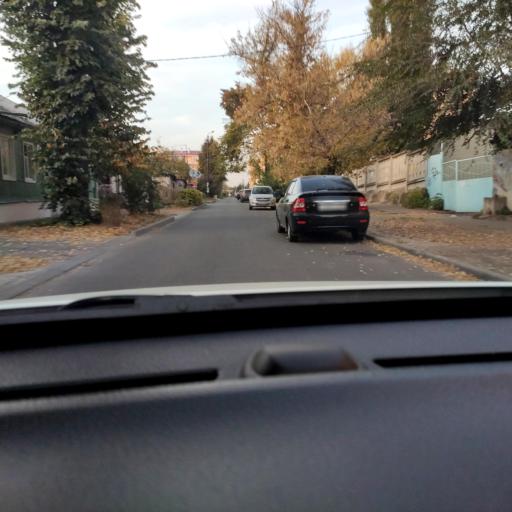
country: RU
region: Voronezj
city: Voronezh
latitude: 51.6853
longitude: 39.2134
